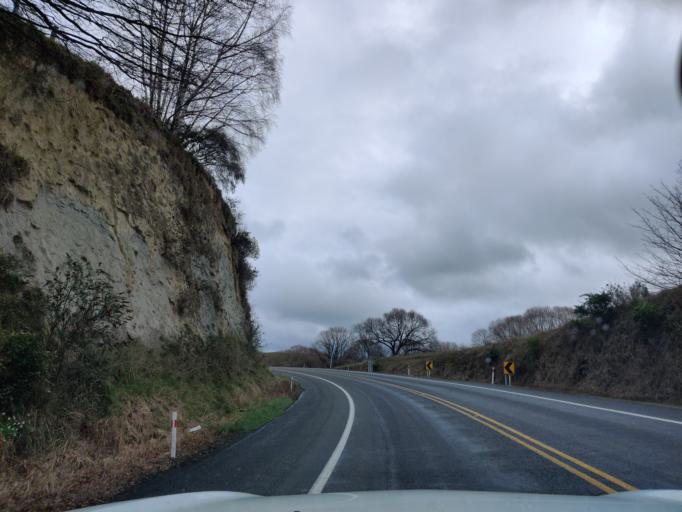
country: NZ
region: Manawatu-Wanganui
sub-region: Ruapehu District
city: Waiouru
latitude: -39.6851
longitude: 175.8060
